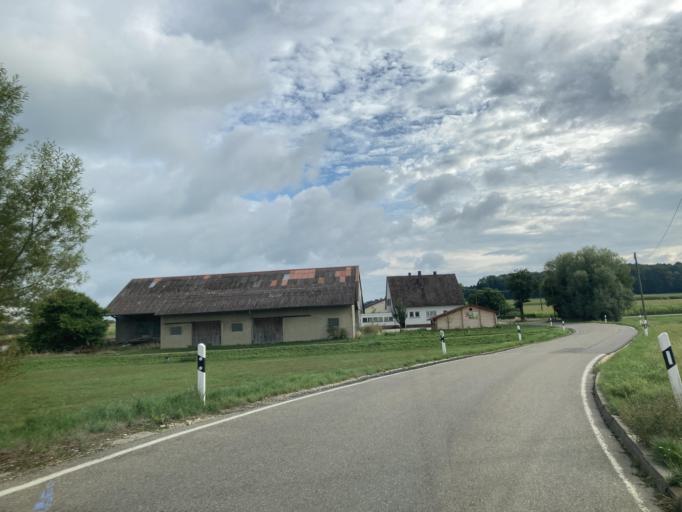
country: DE
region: Bavaria
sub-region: Swabia
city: Bachhagel
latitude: 48.6120
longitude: 10.3078
